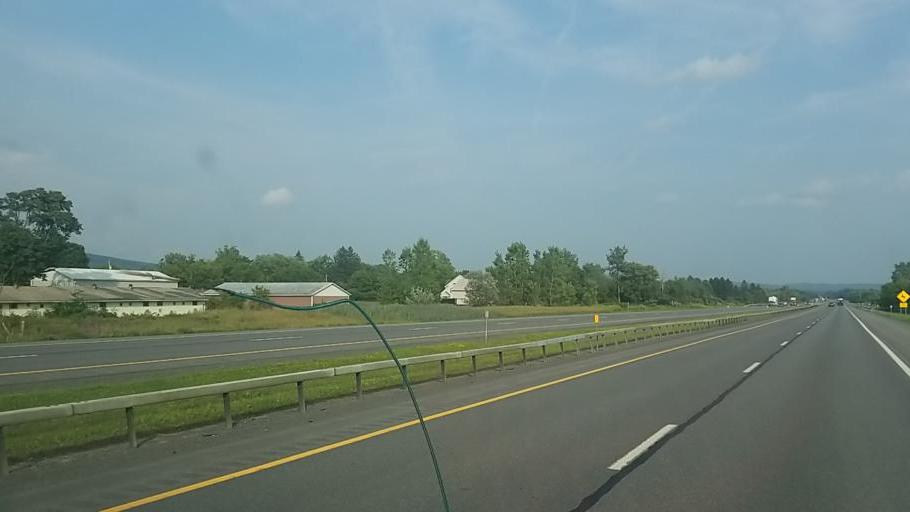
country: US
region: New York
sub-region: Oneida County
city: Utica
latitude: 43.0939
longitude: -75.1443
